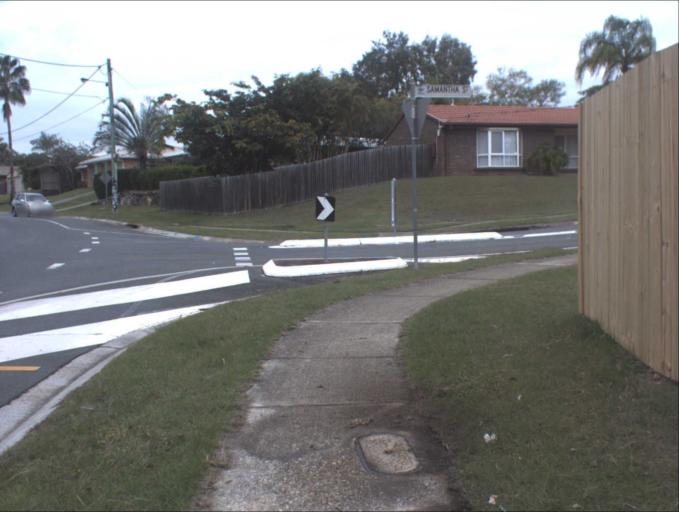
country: AU
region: Queensland
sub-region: Logan
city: Park Ridge South
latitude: -27.6911
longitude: 153.0173
